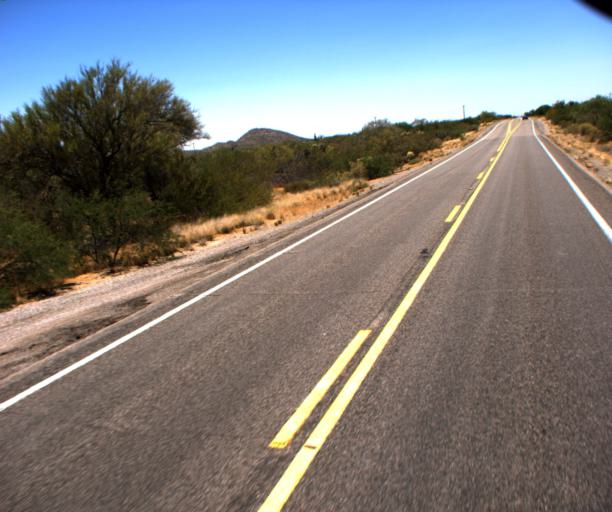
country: US
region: Arizona
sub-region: Pima County
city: Catalina
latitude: 32.7340
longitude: -111.1186
